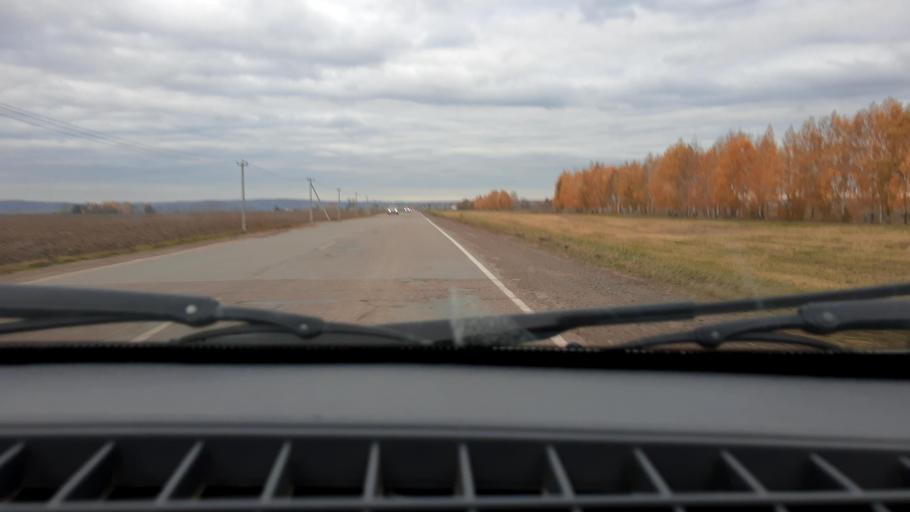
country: RU
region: Bashkortostan
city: Kabakovo
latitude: 54.5412
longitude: 56.0776
